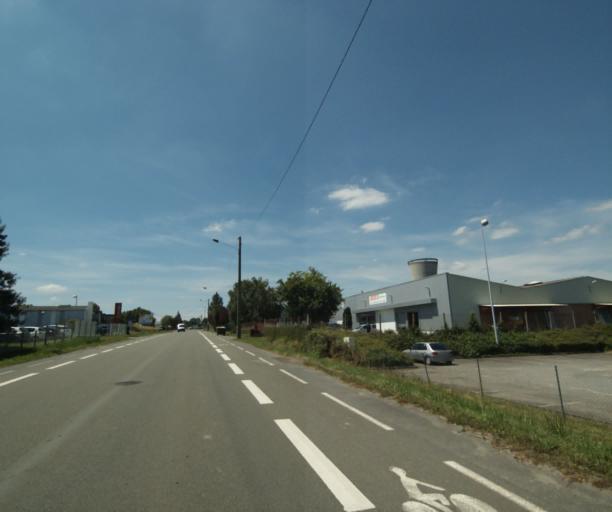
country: FR
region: Pays de la Loire
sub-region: Departement de la Mayenne
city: Laval
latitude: 48.0852
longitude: -0.7452
